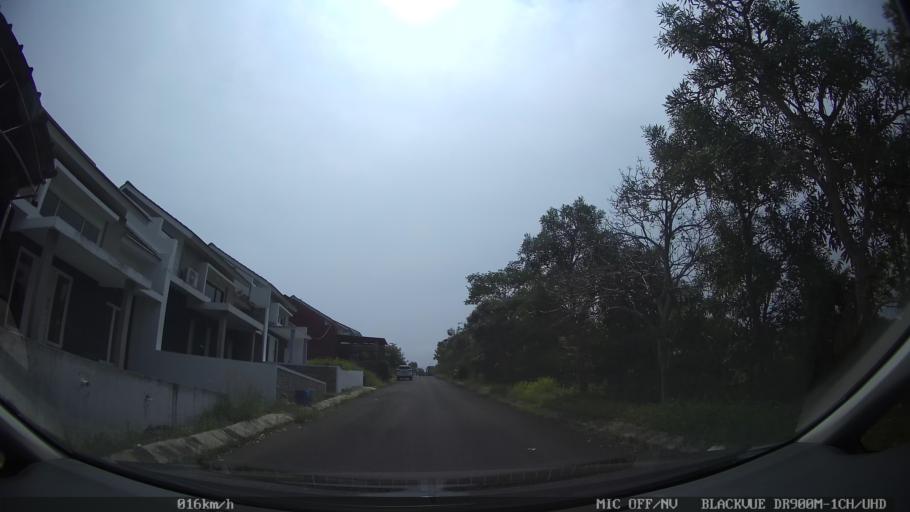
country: ID
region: Lampung
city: Bandarlampung
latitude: -5.4305
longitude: 105.2834
